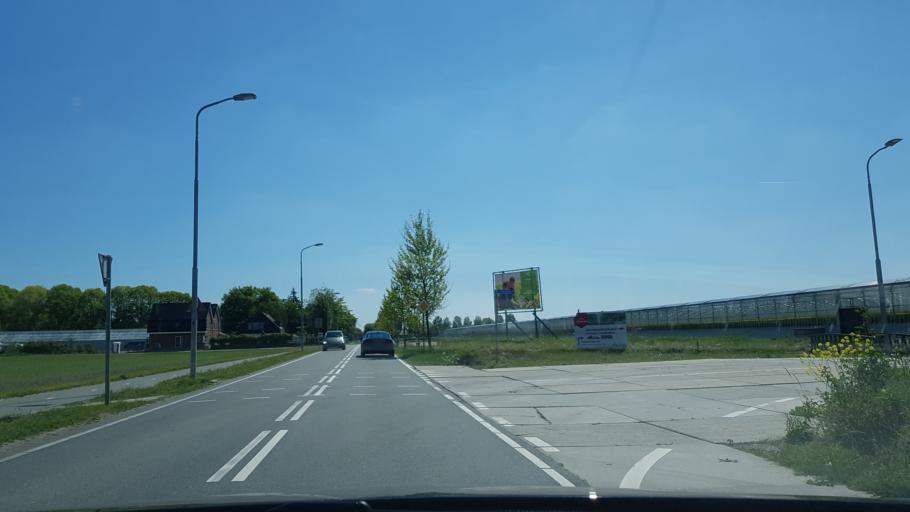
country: NL
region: North Holland
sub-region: Gemeente Haarlemmermeer
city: Hoofddorp
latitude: 52.2650
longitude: 4.7007
